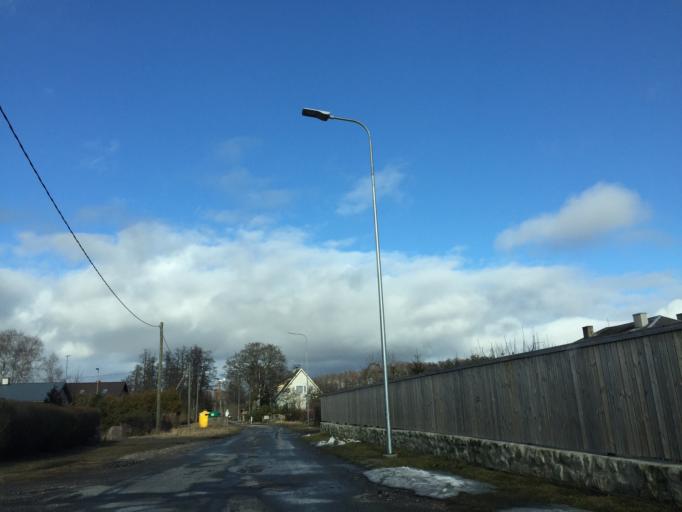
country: EE
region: Laeaene
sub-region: Haapsalu linn
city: Haapsalu
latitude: 58.9311
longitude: 23.5289
